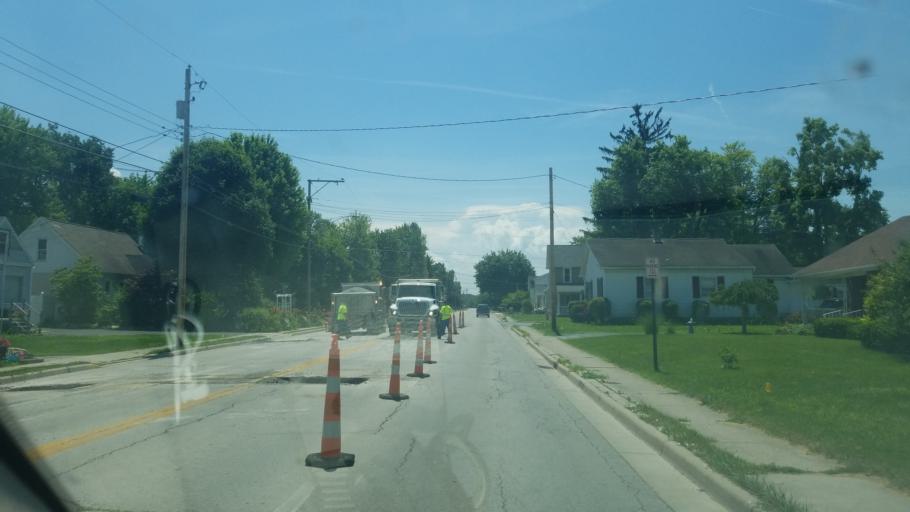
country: US
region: Ohio
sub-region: Hancock County
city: Findlay
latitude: 41.0270
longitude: -83.6412
